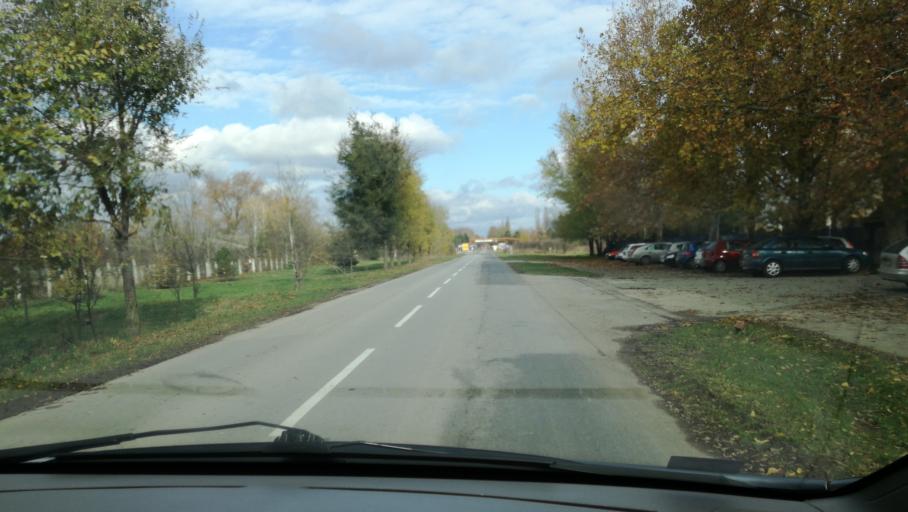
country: RS
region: Autonomna Pokrajina Vojvodina
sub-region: Severnobanatski Okrug
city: Kikinda
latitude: 45.8040
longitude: 20.4435
